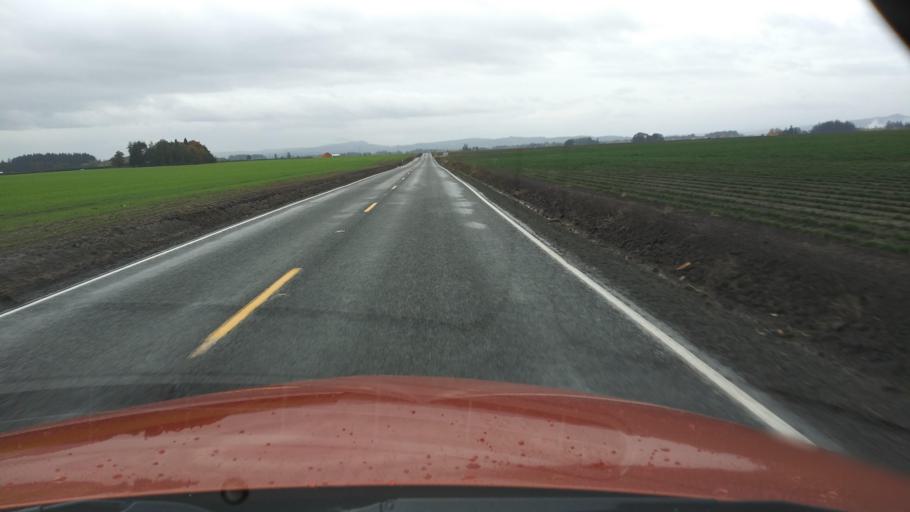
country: US
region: Oregon
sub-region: Washington County
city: North Plains
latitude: 45.5813
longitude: -123.0193
